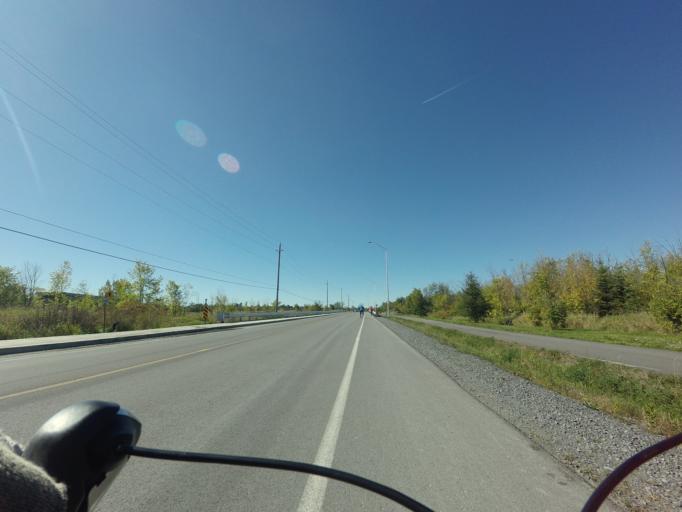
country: CA
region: Ontario
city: Clarence-Rockland
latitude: 45.4968
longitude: -75.4846
